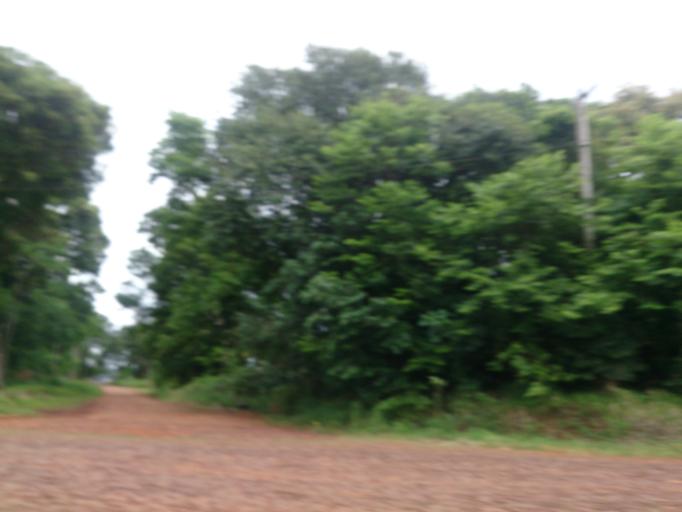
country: AR
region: Misiones
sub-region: Departamento de Obera
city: Obera
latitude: -27.4770
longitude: -55.0961
